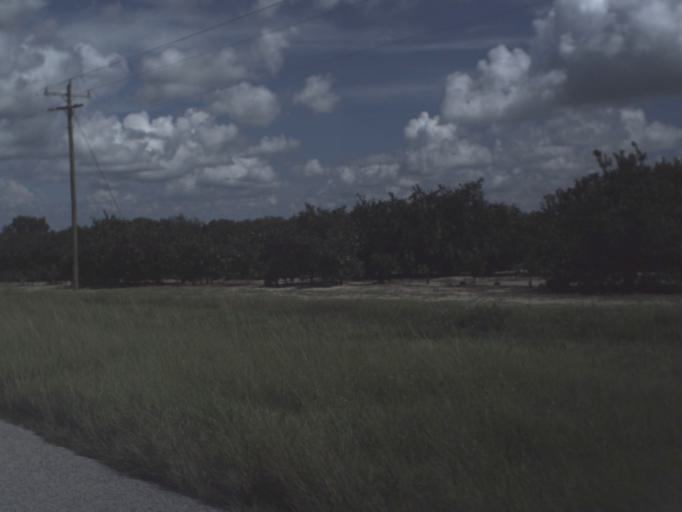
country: US
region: Florida
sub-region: Highlands County
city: Placid Lakes
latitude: 27.1864
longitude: -81.3285
